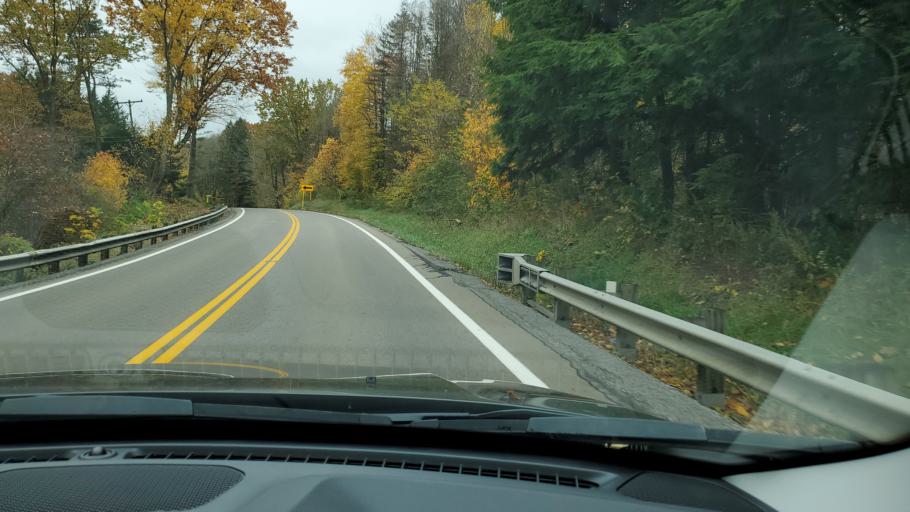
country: US
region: Ohio
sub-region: Columbiana County
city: New Waterford
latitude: 40.8918
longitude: -80.5776
